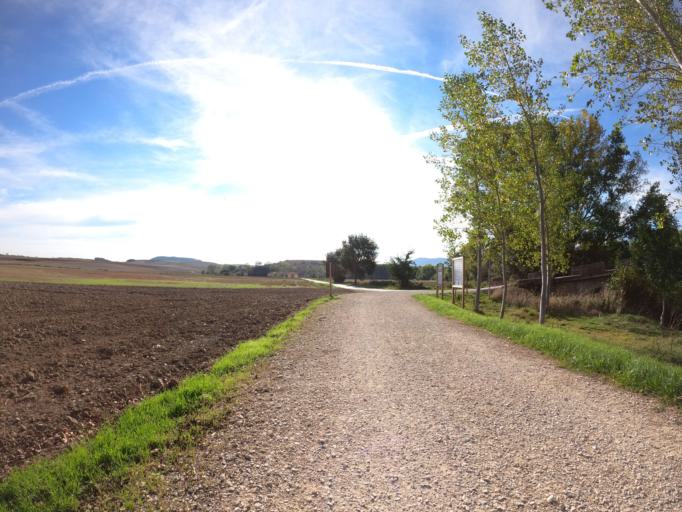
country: ES
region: Navarre
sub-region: Provincia de Navarra
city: Oltza
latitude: 42.8034
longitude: -1.7684
